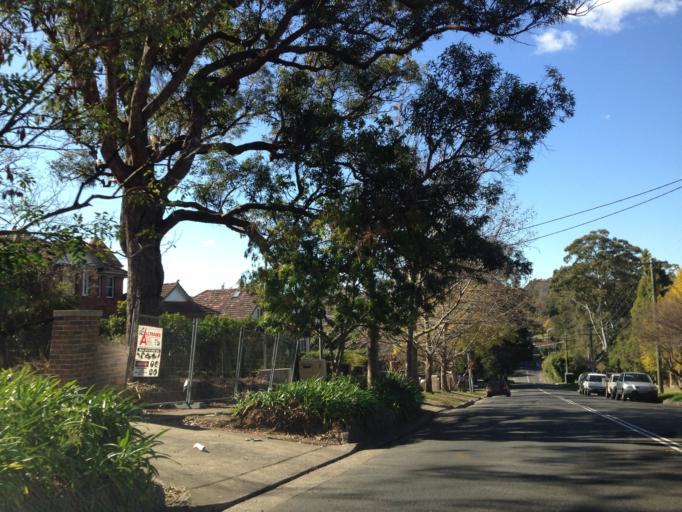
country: AU
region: New South Wales
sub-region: Ku-ring-gai
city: Killara
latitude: -33.7615
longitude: 151.1640
